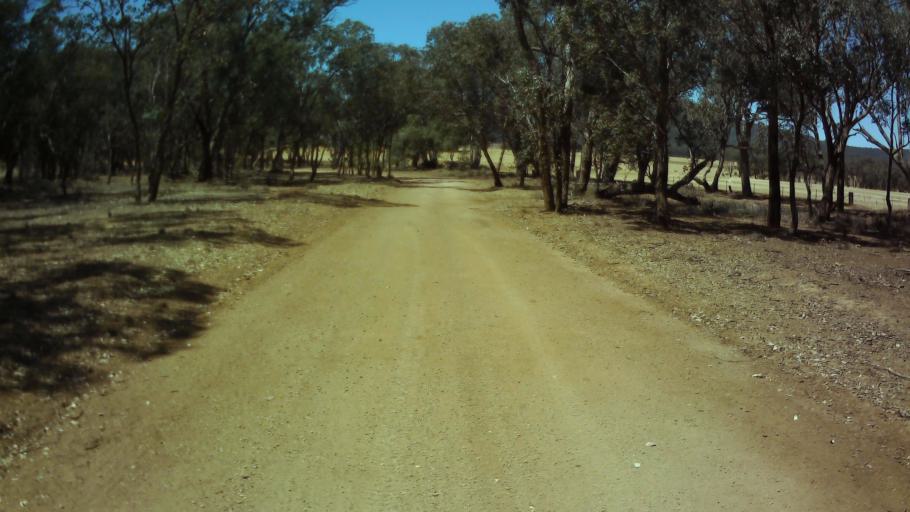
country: AU
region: New South Wales
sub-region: Weddin
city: Grenfell
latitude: -33.9552
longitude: 148.0844
